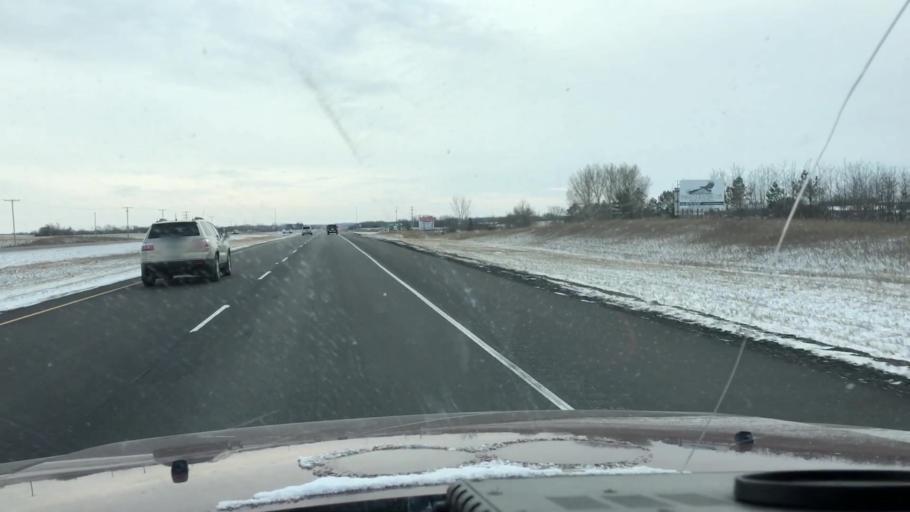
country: CA
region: Saskatchewan
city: Saskatoon
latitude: 52.0303
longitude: -106.5839
